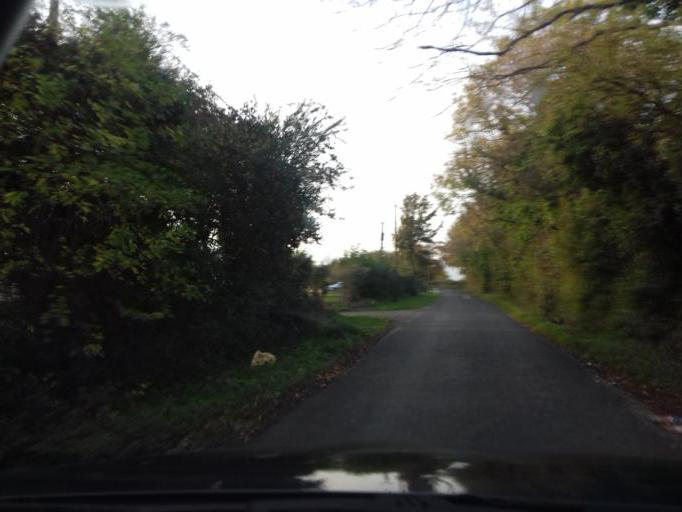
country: IE
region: Leinster
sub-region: An Mhi
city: Dunboyne
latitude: 53.3874
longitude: -6.4656
